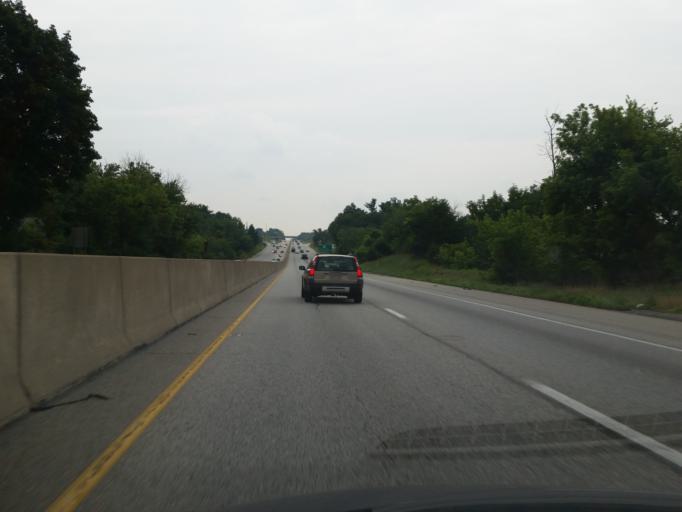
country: US
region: Pennsylvania
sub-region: York County
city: Manchester
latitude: 40.0747
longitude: -76.7605
